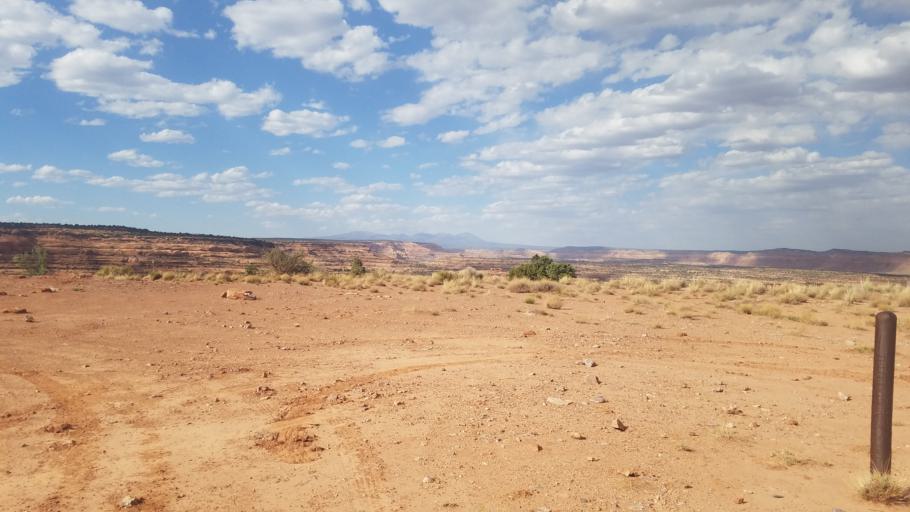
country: US
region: Utah
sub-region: San Juan County
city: Blanding
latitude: 37.3796
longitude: -109.7418
